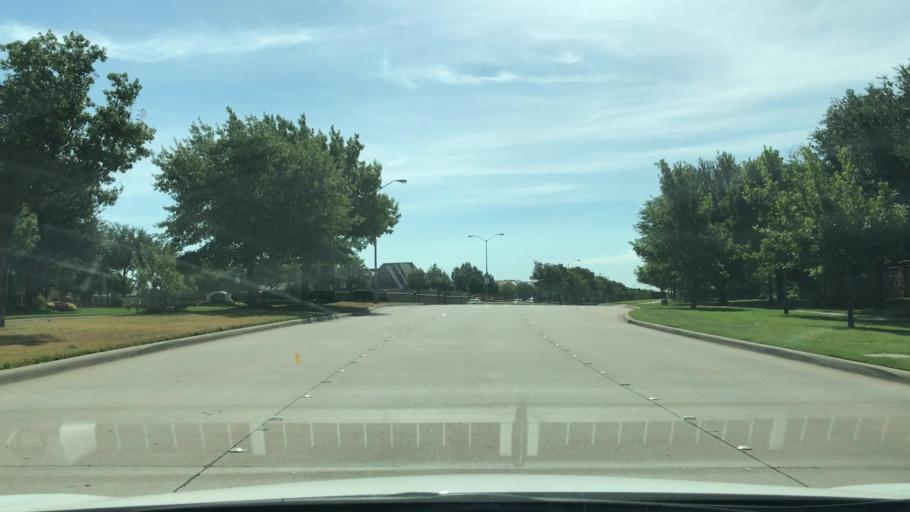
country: US
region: Texas
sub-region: Denton County
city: The Colony
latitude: 33.0691
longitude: -96.8445
